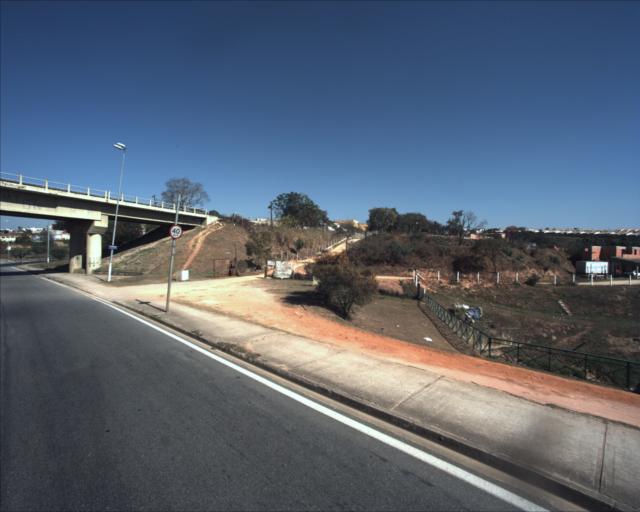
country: BR
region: Sao Paulo
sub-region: Sorocaba
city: Sorocaba
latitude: -23.4898
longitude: -47.4950
